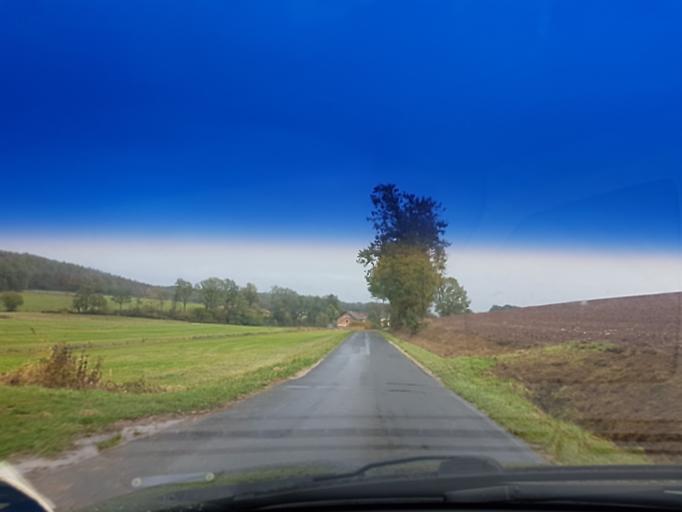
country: DE
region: Bavaria
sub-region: Regierungsbezirk Mittelfranken
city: Wachenroth
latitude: 49.7611
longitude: 10.6838
